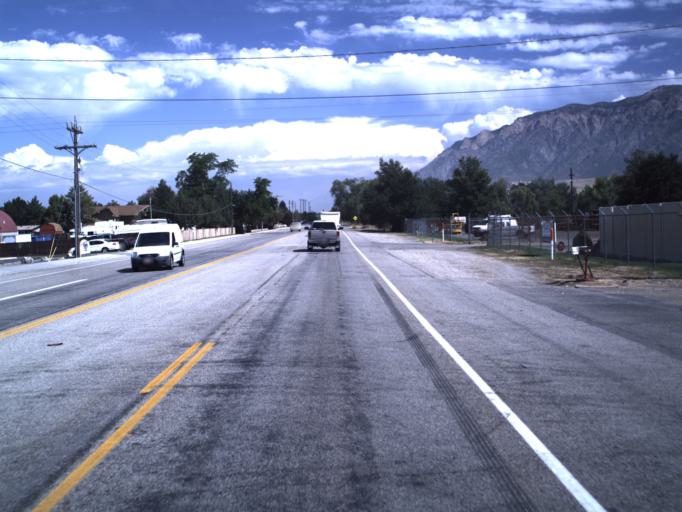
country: US
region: Utah
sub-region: Weber County
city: Farr West
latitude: 41.2769
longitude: -112.0281
